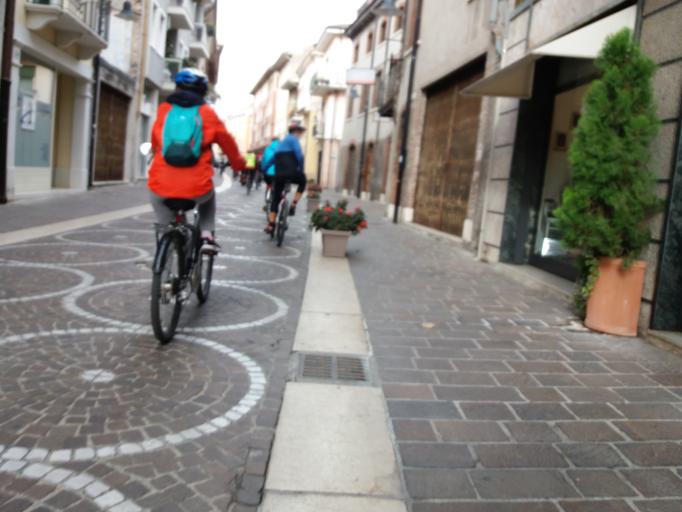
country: IT
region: Veneto
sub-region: Provincia di Verona
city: Bussolengo
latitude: 45.4737
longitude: 10.8502
